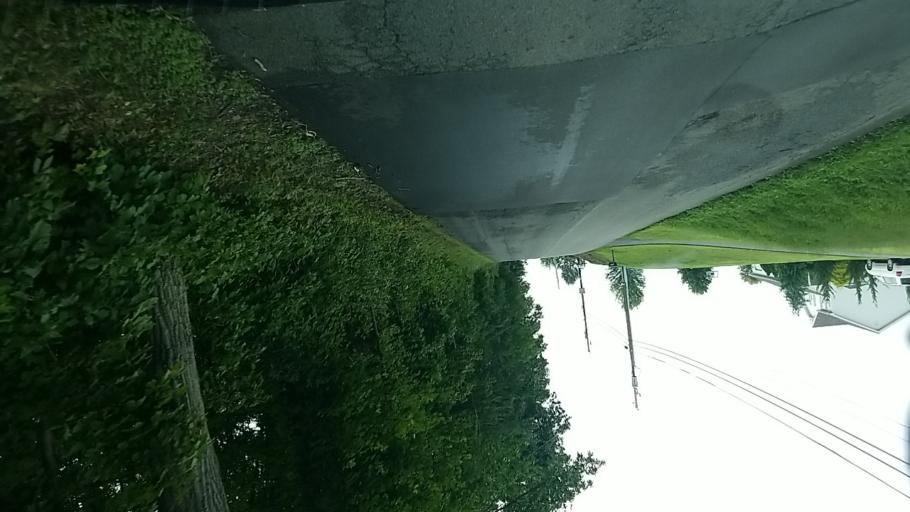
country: US
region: Pennsylvania
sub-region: Dauphin County
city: Matamoras
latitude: 40.4956
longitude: -76.9202
